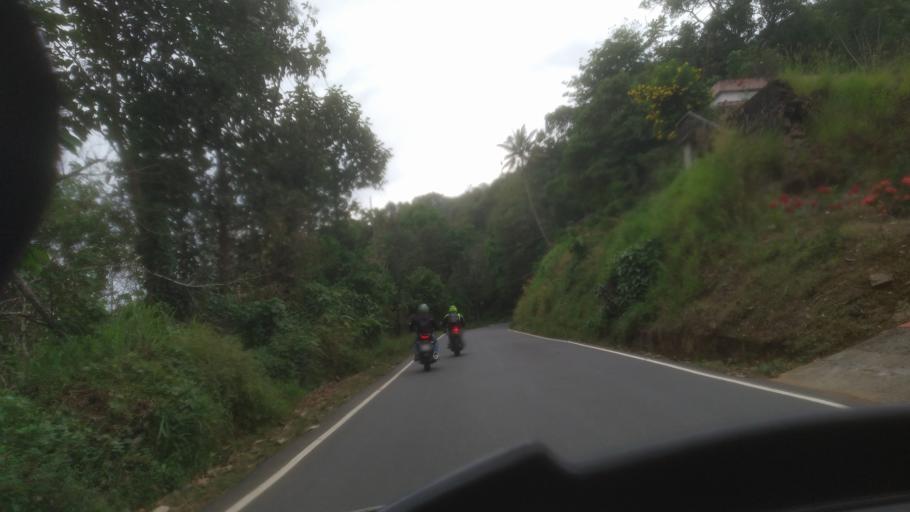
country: IN
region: Kerala
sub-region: Idukki
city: Idukki
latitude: 9.9577
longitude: 77.0106
